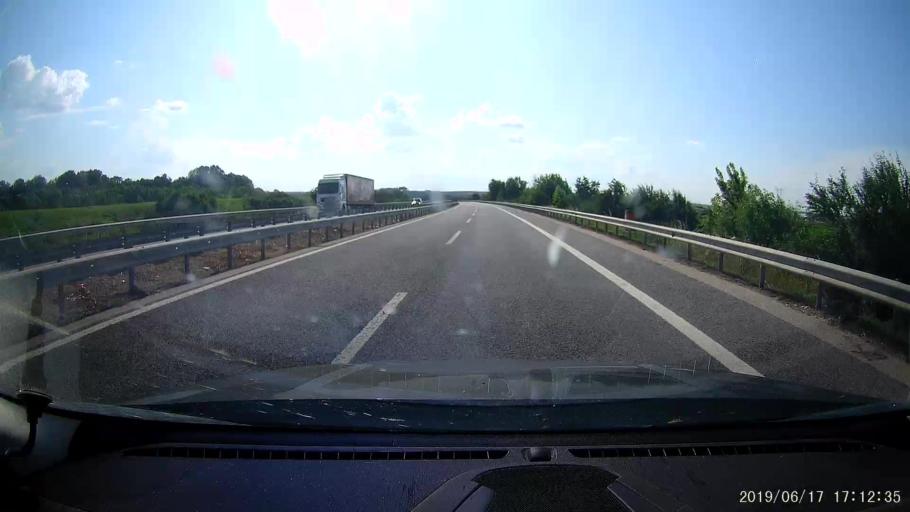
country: TR
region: Edirne
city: Edirne
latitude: 41.7004
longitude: 26.5595
